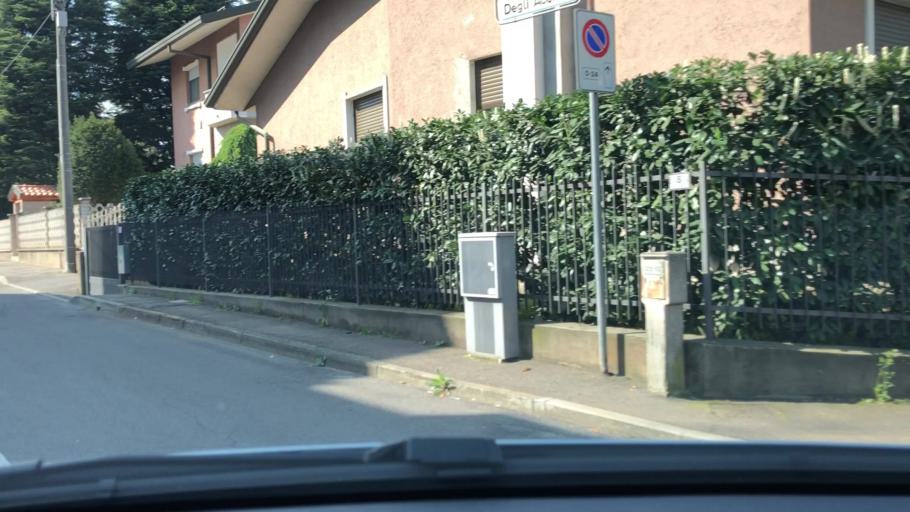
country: IT
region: Lombardy
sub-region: Provincia di Monza e Brianza
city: Barlassina
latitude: 45.6424
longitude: 9.1272
